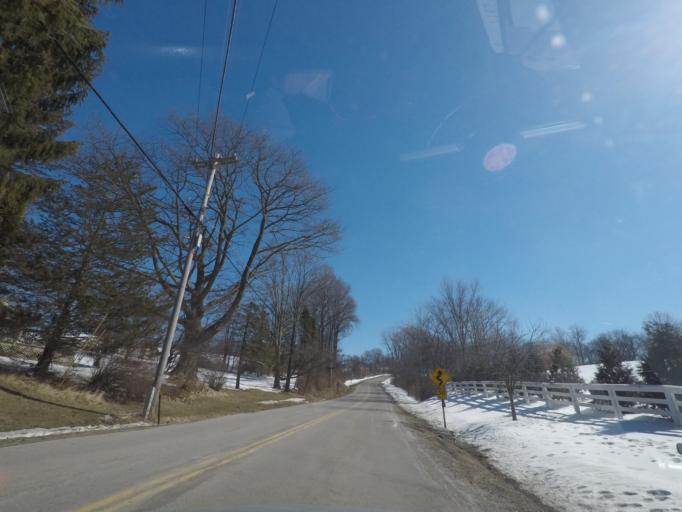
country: US
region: New York
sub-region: Saratoga County
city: Saratoga Springs
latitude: 43.0434
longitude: -73.7098
